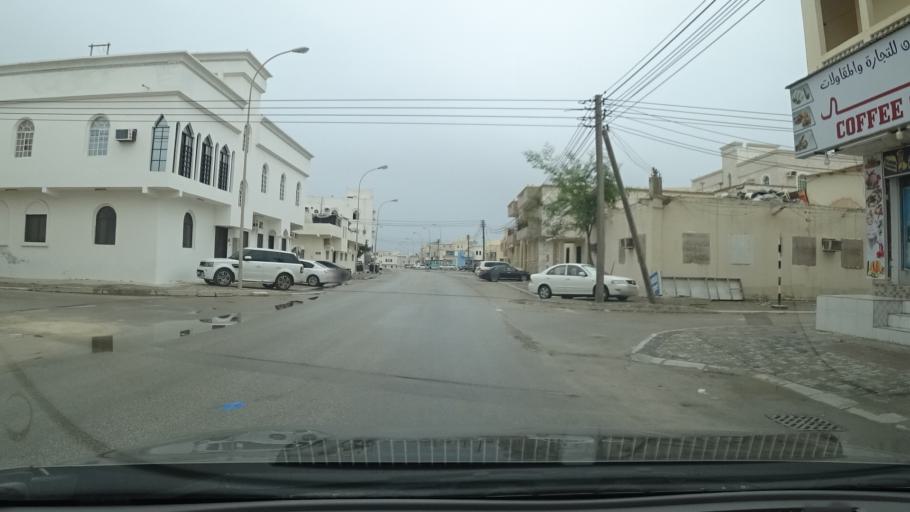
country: OM
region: Zufar
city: Salalah
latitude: 17.0233
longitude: 54.1589
